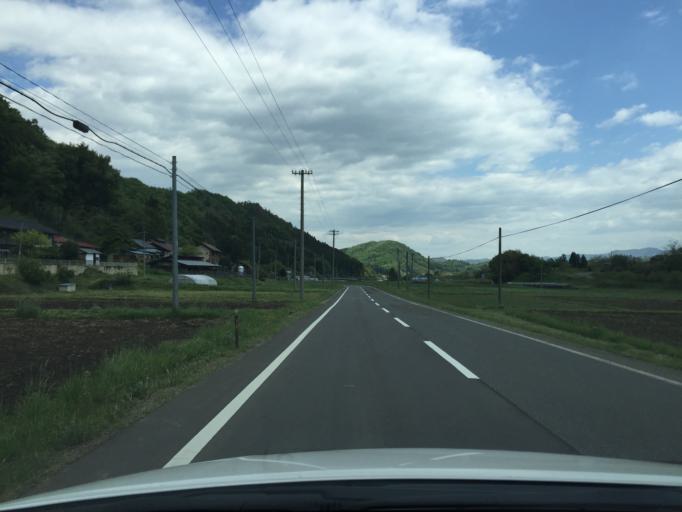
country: JP
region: Fukushima
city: Hobaramachi
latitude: 37.7538
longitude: 140.5681
